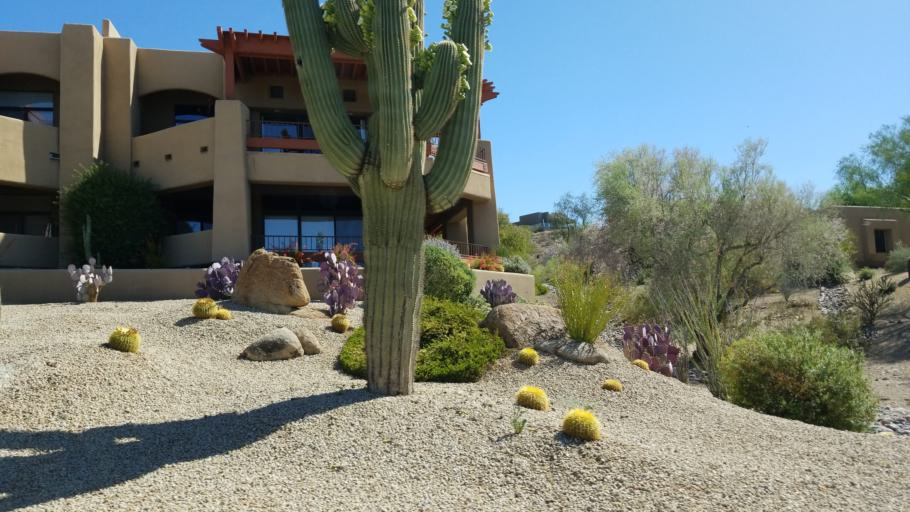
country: US
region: Arizona
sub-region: Maricopa County
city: Fountain Hills
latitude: 33.6049
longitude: -111.7119
